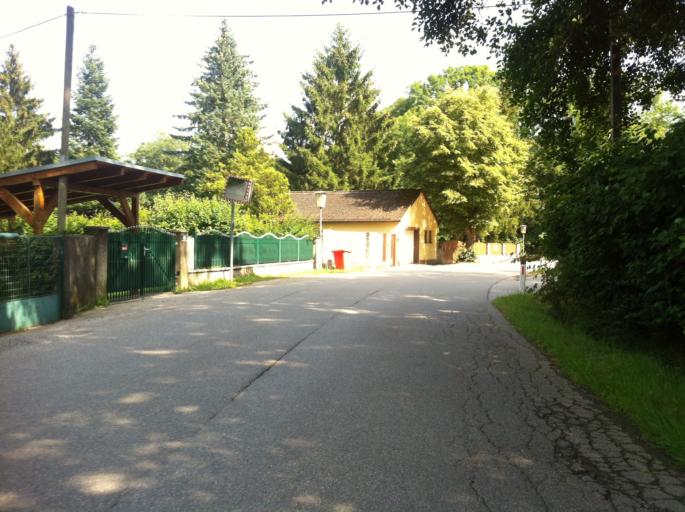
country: AT
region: Lower Austria
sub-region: Politischer Bezirk Wien-Umgebung
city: Purkersdorf
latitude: 48.1844
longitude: 16.1763
